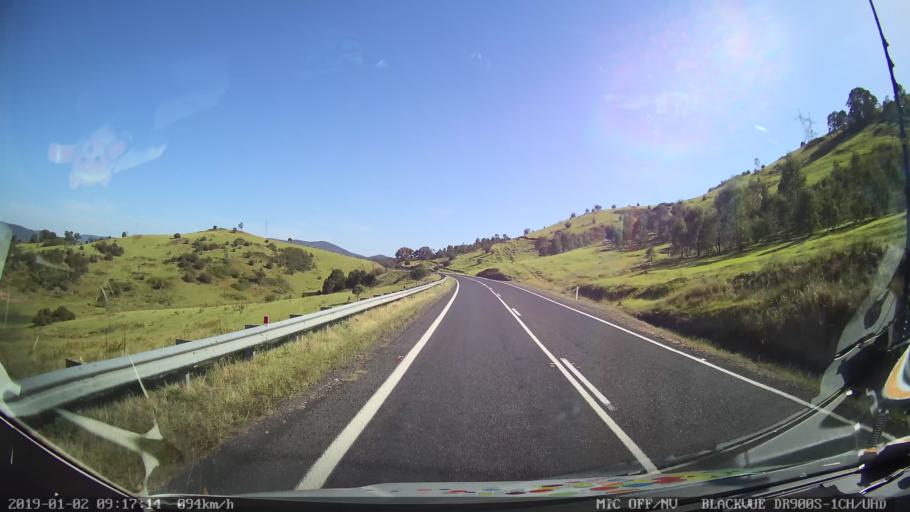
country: AU
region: New South Wales
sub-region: Tumut Shire
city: Tumut
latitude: -35.4436
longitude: 148.2869
